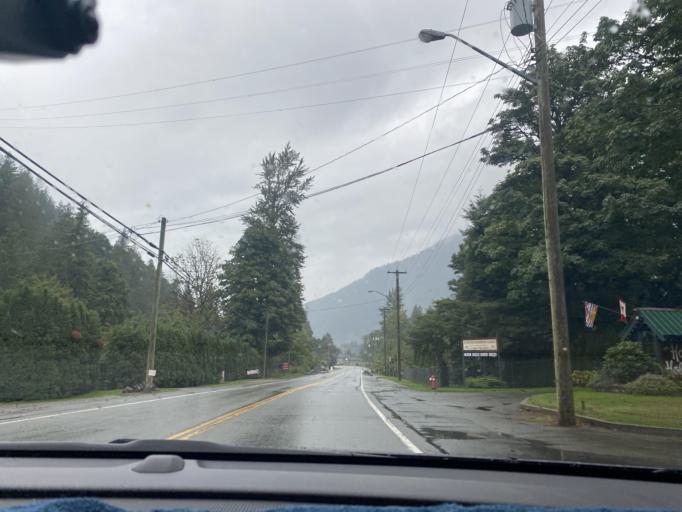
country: CA
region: British Columbia
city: Agassiz
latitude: 49.2819
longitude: -121.7827
